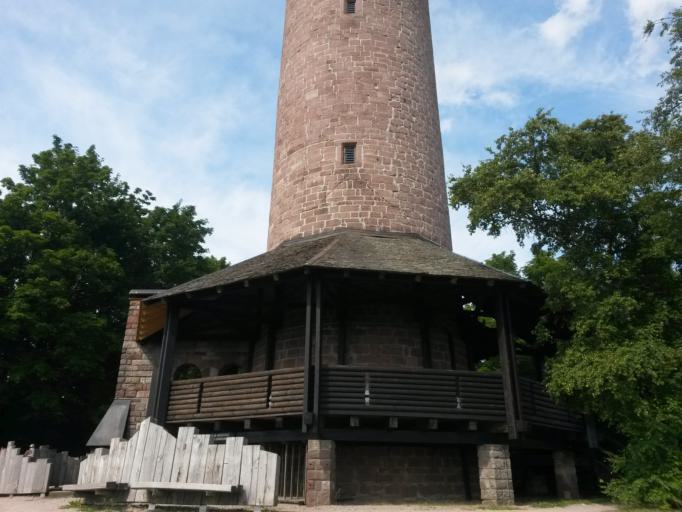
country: DE
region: Baden-Wuerttemberg
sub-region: Karlsruhe Region
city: Baden-Baden
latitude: 48.7643
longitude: 8.2803
